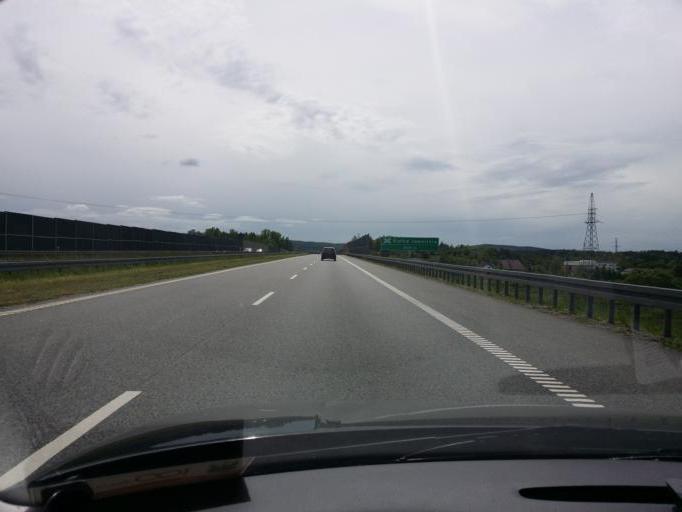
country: PL
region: Swietokrzyskie
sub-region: Powiat kielecki
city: Miedziana Gora
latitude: 50.8861
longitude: 20.5237
